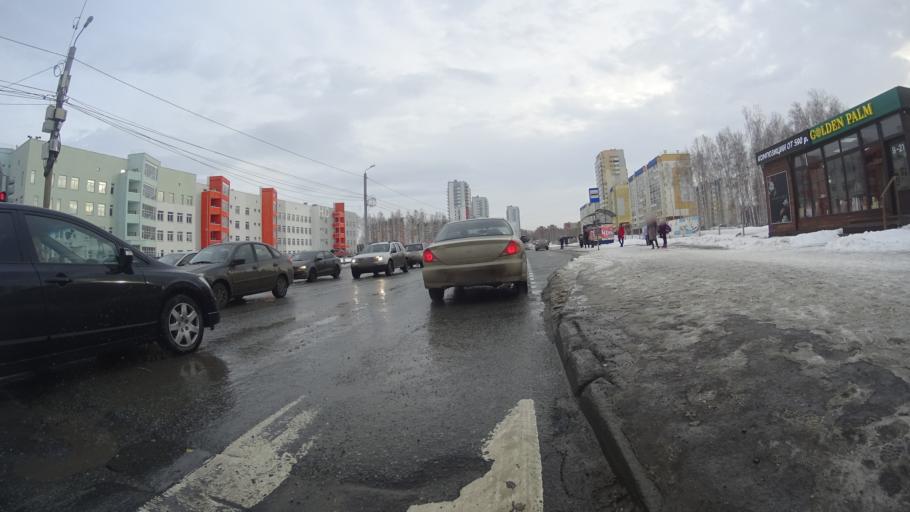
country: RU
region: Chelyabinsk
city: Roshchino
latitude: 55.2072
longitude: 61.2843
